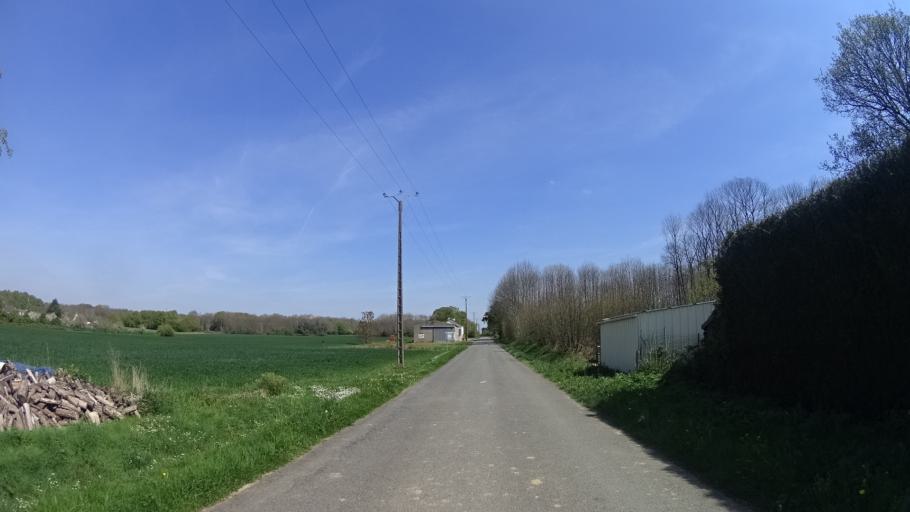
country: FR
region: Pays de la Loire
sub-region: Departement de la Loire-Atlantique
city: Fegreac
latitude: 47.5961
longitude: -2.0680
